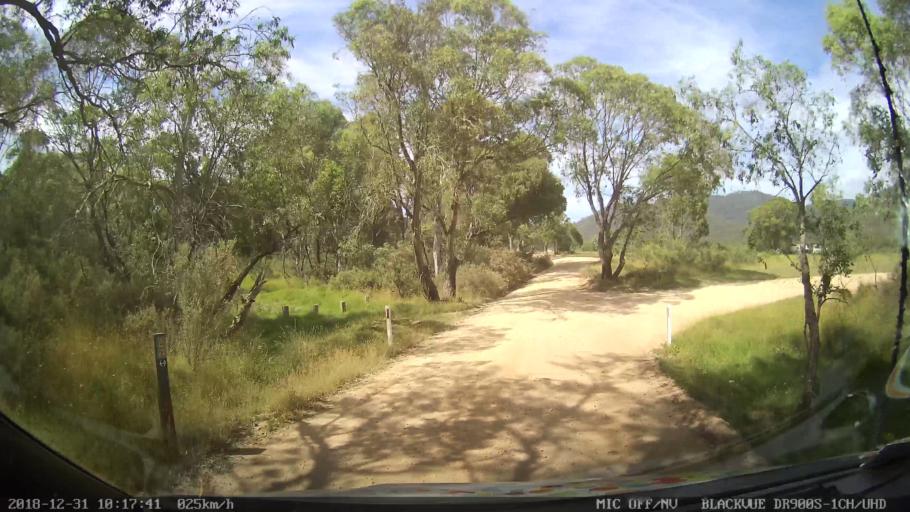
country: AU
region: New South Wales
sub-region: Snowy River
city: Jindabyne
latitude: -36.5409
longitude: 148.1347
